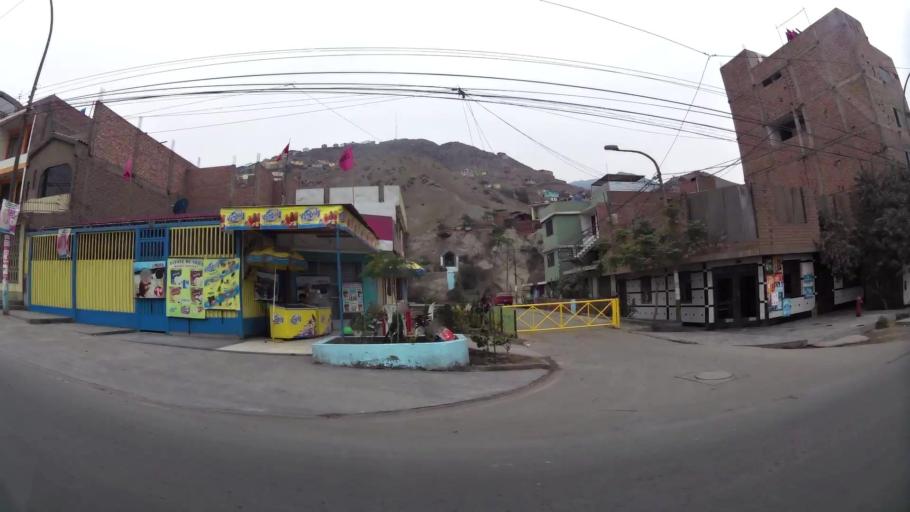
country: PE
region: Lima
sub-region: Lima
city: Independencia
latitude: -11.9846
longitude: -76.9943
